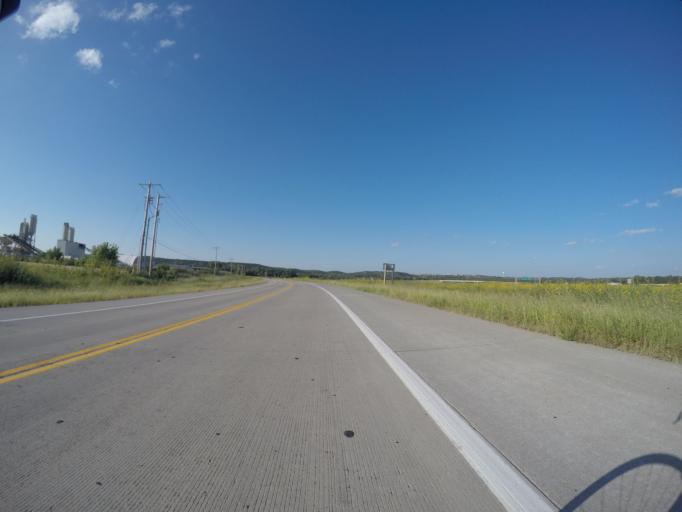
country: US
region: Kansas
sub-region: Riley County
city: Ogden
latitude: 39.1492
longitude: -96.6492
